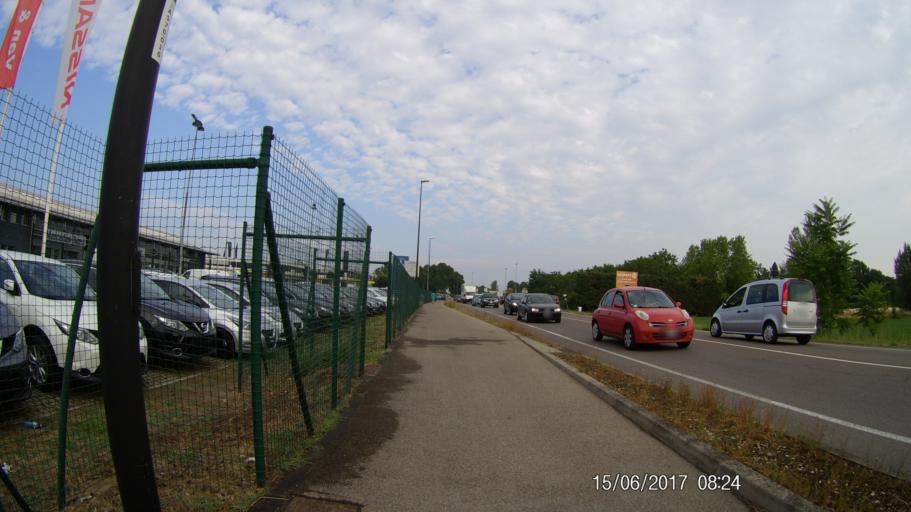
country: IT
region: Emilia-Romagna
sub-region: Provincia di Reggio Emilia
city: Roncocesi
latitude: 44.7224
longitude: 10.5623
